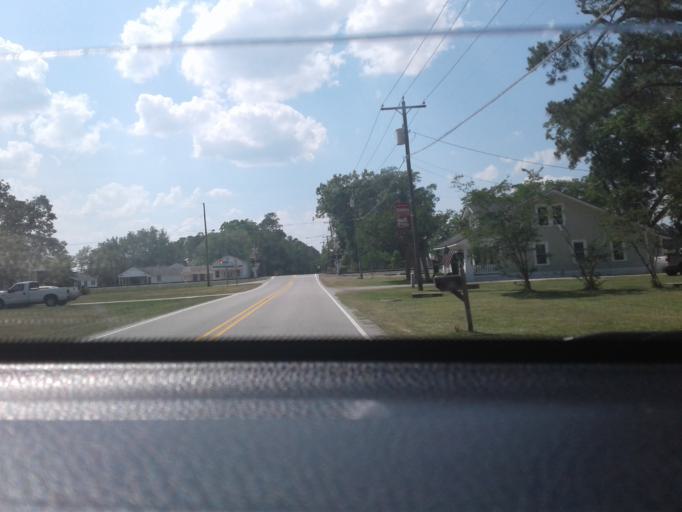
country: US
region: North Carolina
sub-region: Harnett County
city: Erwin
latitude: 35.2172
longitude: -78.6797
